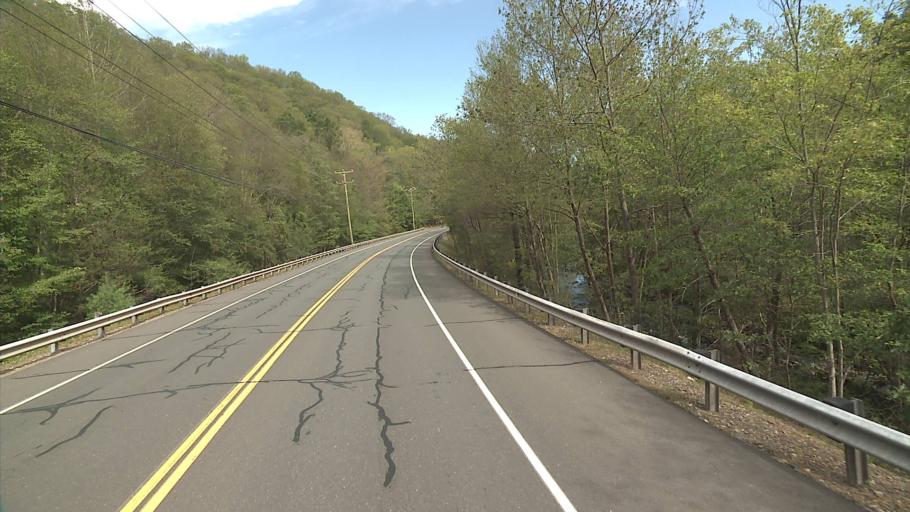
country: US
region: Connecticut
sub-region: Tolland County
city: Stafford Springs
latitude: 41.9313
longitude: -72.3094
